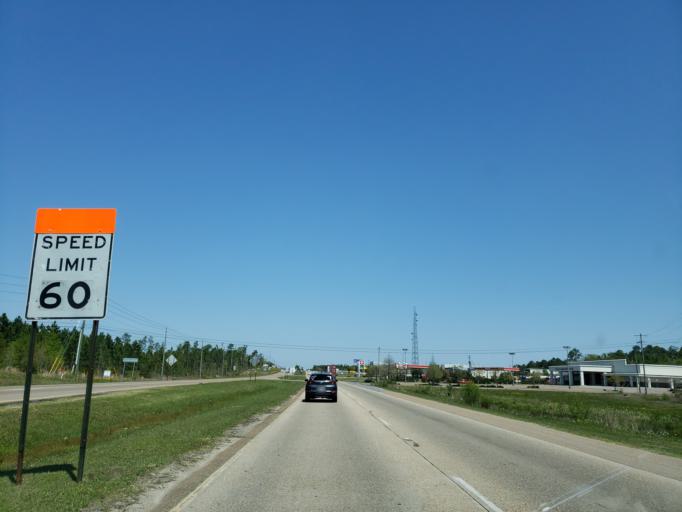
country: US
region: Mississippi
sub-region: Harrison County
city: Lyman
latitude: 30.4826
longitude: -89.1033
